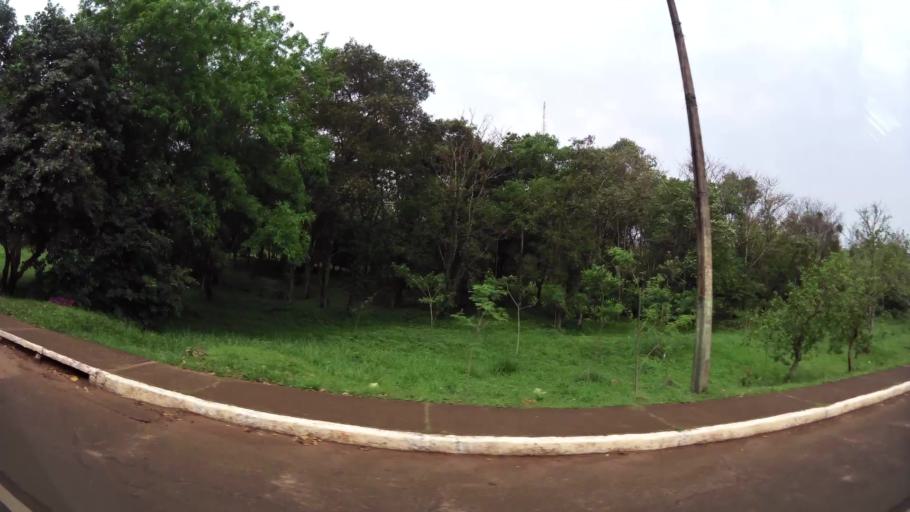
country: PY
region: Alto Parana
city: Presidente Franco
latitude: -25.5486
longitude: -54.6108
